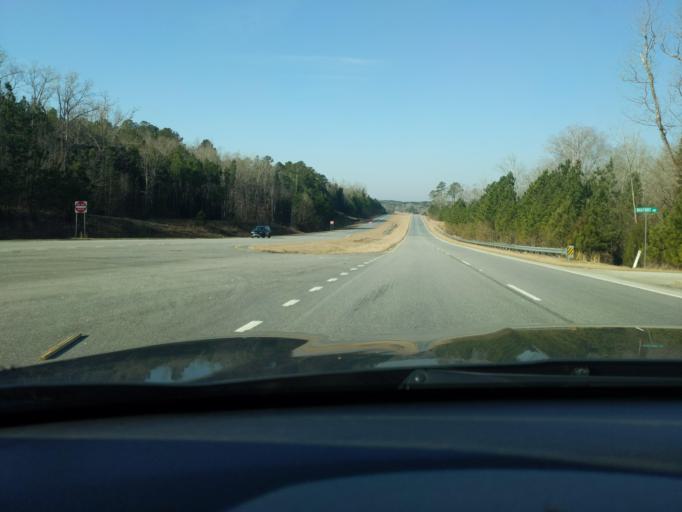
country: US
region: South Carolina
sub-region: Abbeville County
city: Calhoun Falls
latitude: 34.1111
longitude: -82.4989
